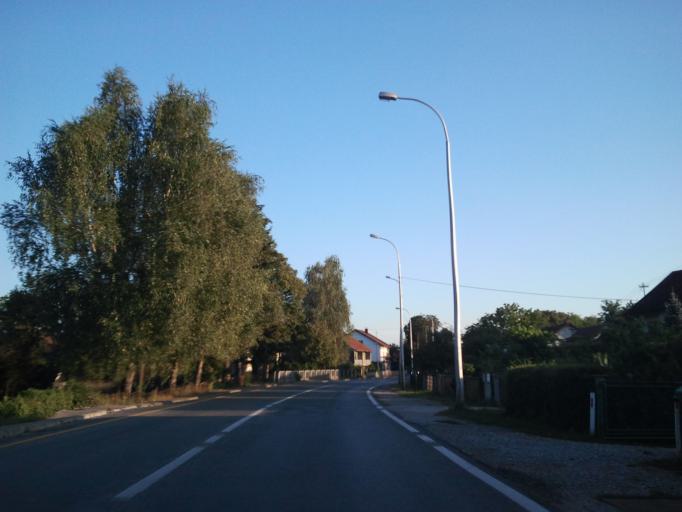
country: HR
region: Sisacko-Moslavacka
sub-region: Grad Sisak
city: Sisak
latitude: 45.4506
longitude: 16.3702
